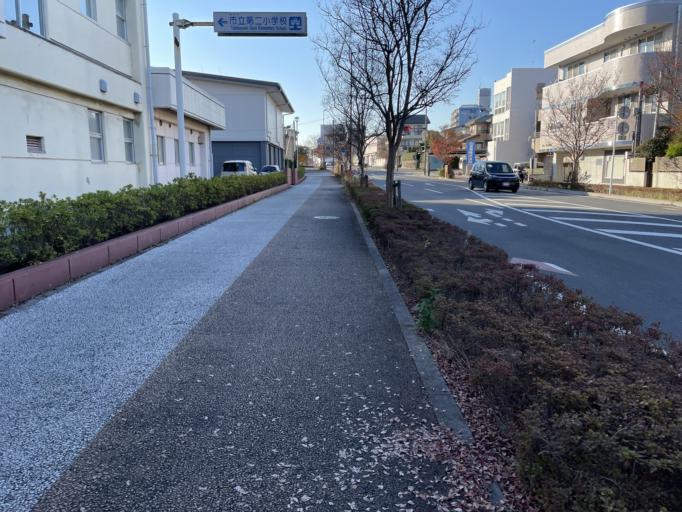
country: JP
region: Gunma
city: Tatebayashi
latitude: 36.2454
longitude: 139.5367
